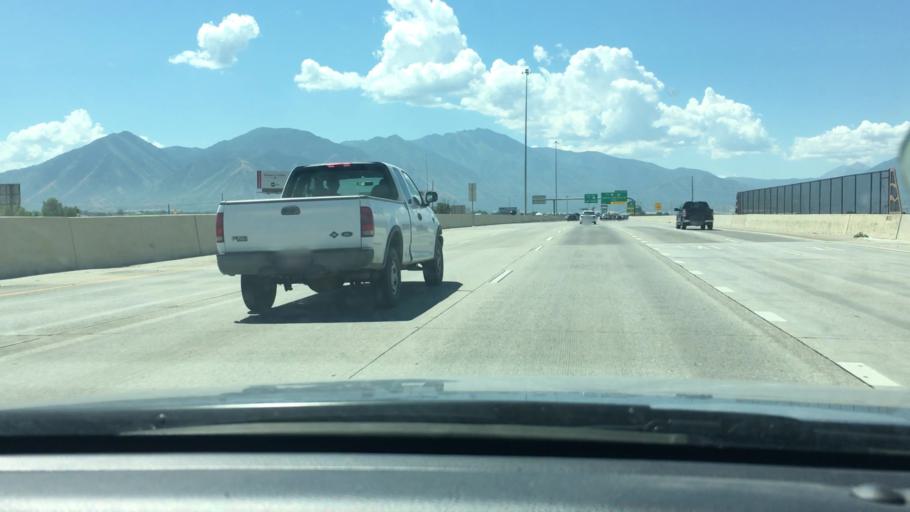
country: US
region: Utah
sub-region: Utah County
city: Spanish Fork
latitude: 40.1383
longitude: -111.6471
